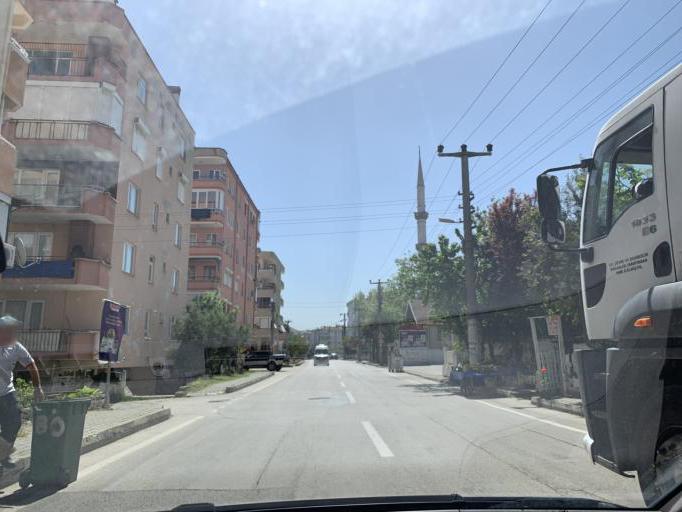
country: TR
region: Bursa
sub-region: Mudanya
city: Mudanya
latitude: 40.3587
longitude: 28.9149
